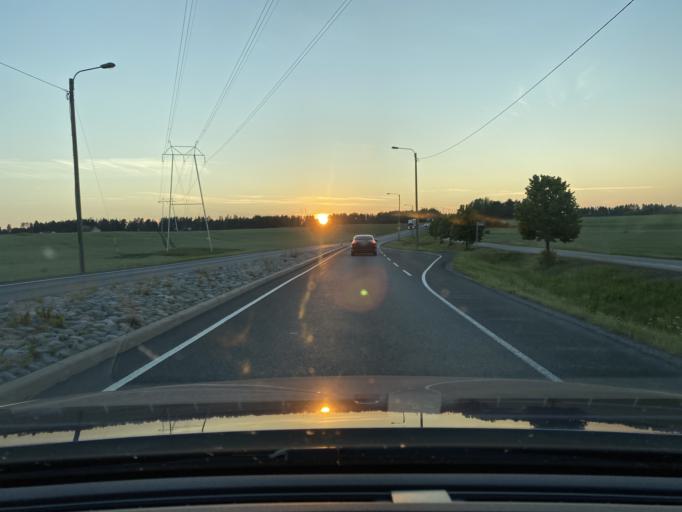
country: FI
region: Pirkanmaa
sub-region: Luoteis-Pirkanmaa
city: Ikaalinen
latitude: 61.7596
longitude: 23.0271
